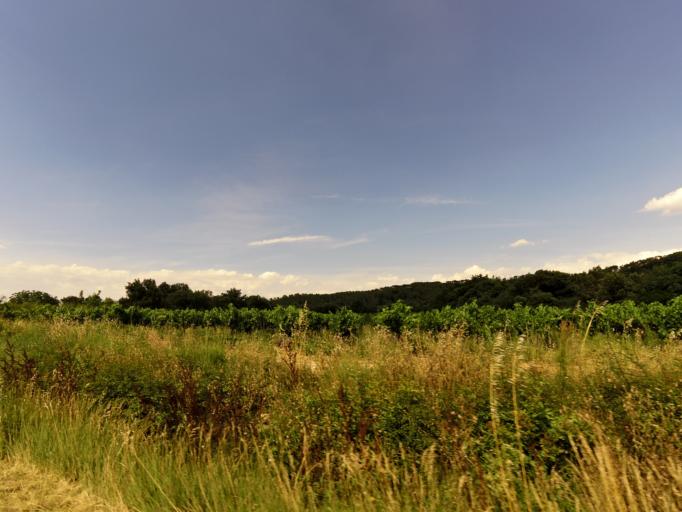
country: FR
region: Languedoc-Roussillon
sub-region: Departement du Gard
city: Quissac
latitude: 43.8483
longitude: 4.0194
